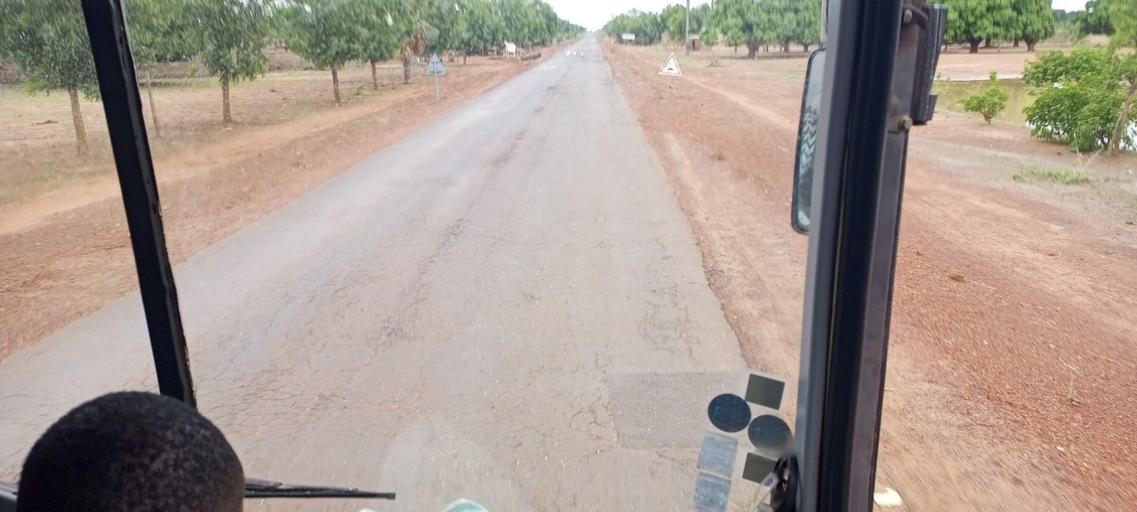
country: ML
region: Sikasso
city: Koutiala
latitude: 12.5797
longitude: -5.6099
